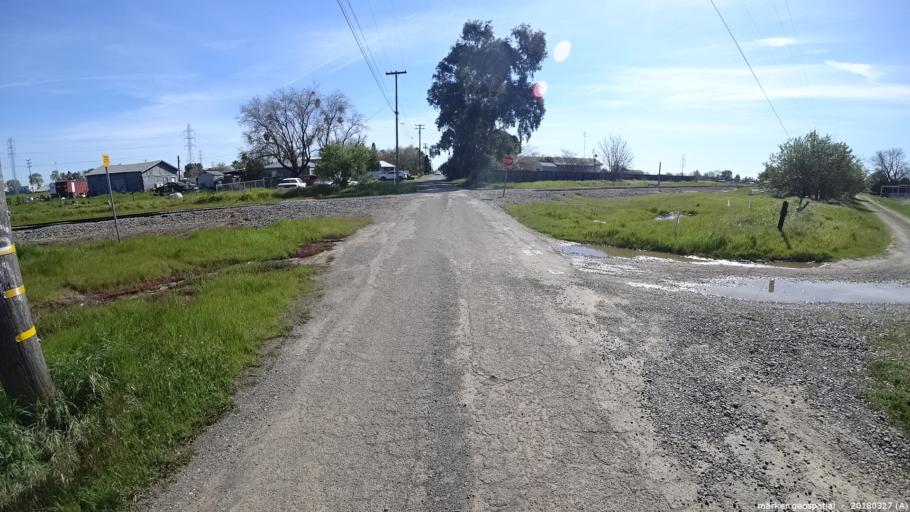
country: US
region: California
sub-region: Sacramento County
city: Florin
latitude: 38.5071
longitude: -121.3687
